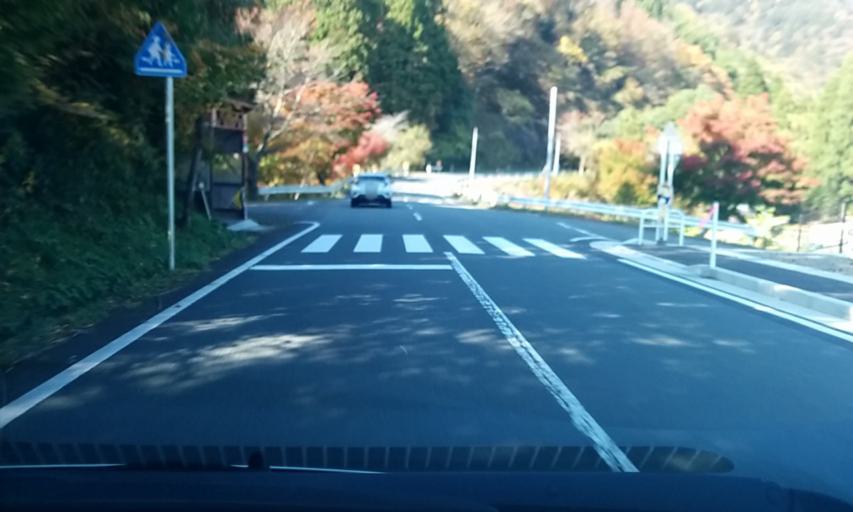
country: JP
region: Kyoto
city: Kameoka
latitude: 35.2413
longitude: 135.5598
